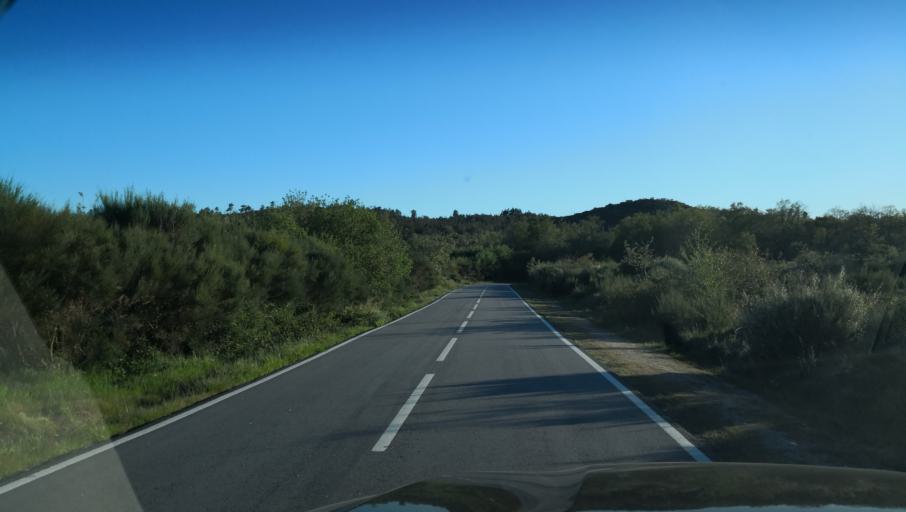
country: PT
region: Vila Real
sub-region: Sabrosa
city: Sabrosa
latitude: 41.3639
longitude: -7.6325
